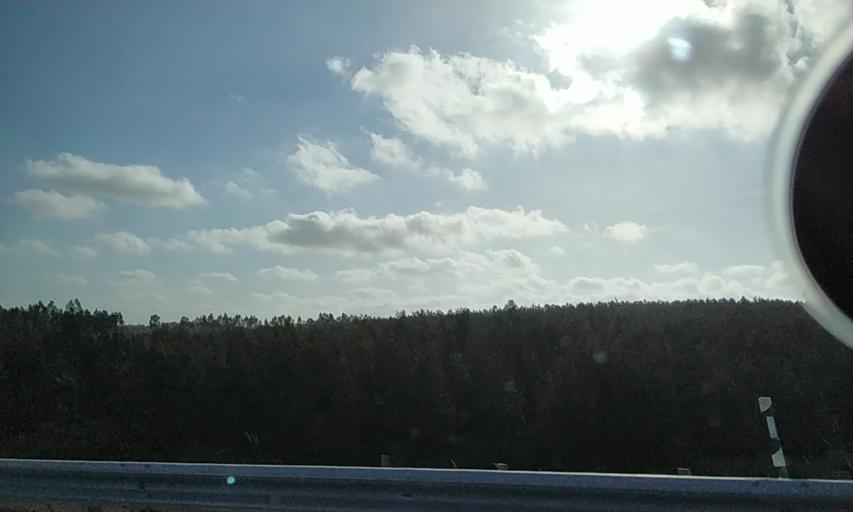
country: PT
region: Lisbon
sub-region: Torres Vedras
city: A dos Cunhados
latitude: 39.1788
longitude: -9.2042
